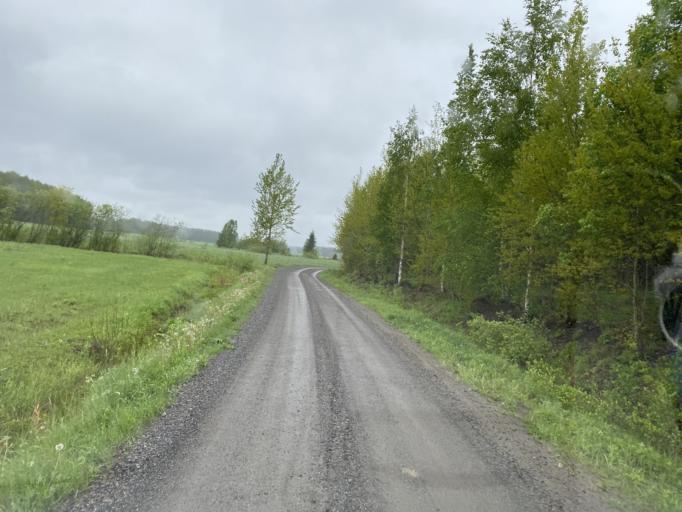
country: FI
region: Pirkanmaa
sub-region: Etelae-Pirkanmaa
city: Urjala
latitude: 60.9573
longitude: 23.5996
